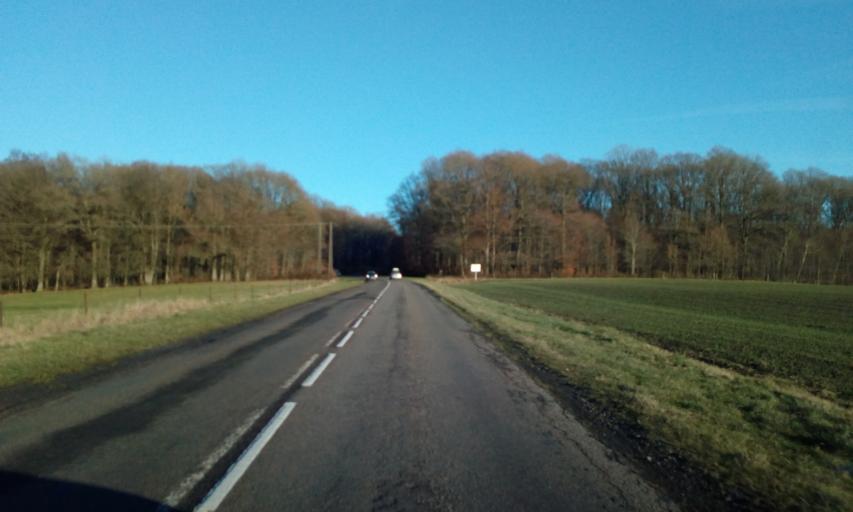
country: FR
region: Champagne-Ardenne
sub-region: Departement des Ardennes
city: Signy-le-Petit
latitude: 49.7719
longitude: 4.3542
